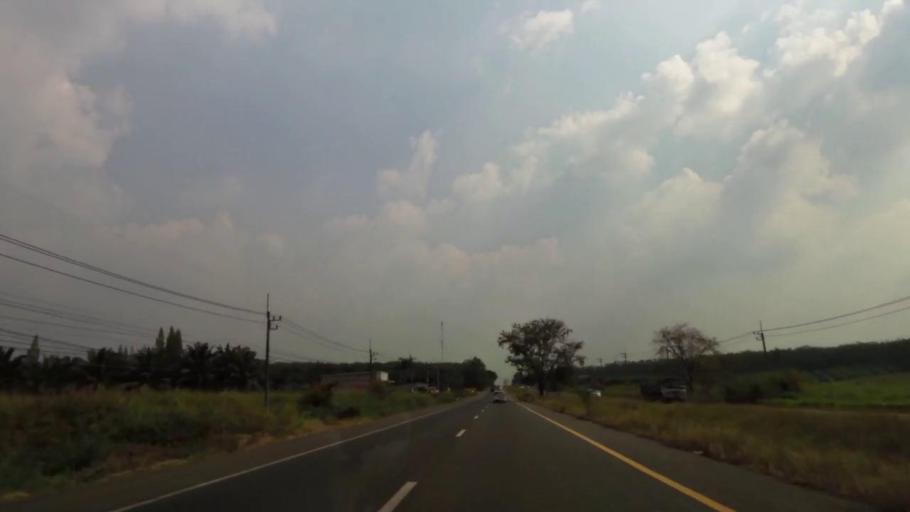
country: TH
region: Chon Buri
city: Nong Yai
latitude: 13.1148
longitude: 101.3728
